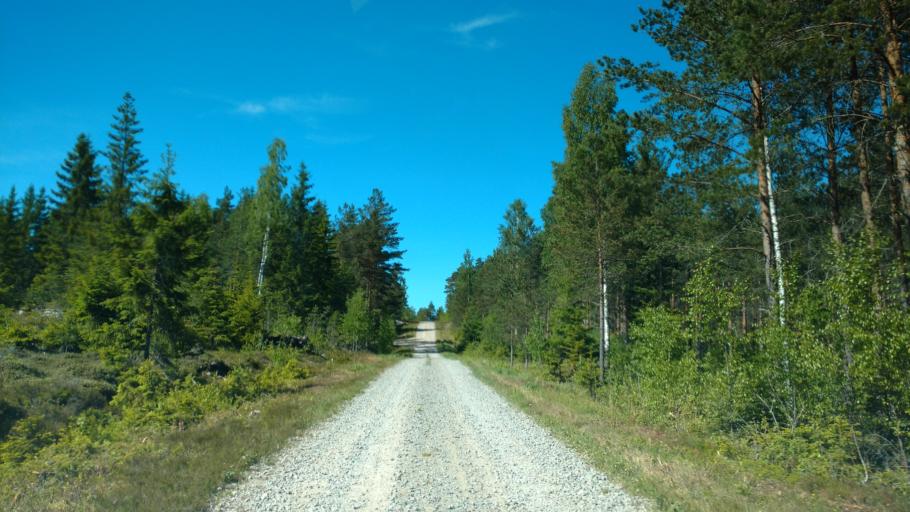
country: FI
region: Varsinais-Suomi
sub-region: Salo
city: Halikko
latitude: 60.4375
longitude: 22.9708
